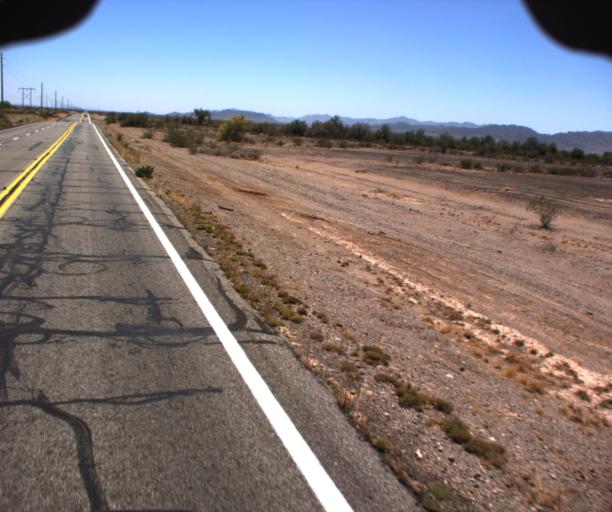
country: US
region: Arizona
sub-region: La Paz County
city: Quartzsite
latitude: 33.7740
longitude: -114.2170
